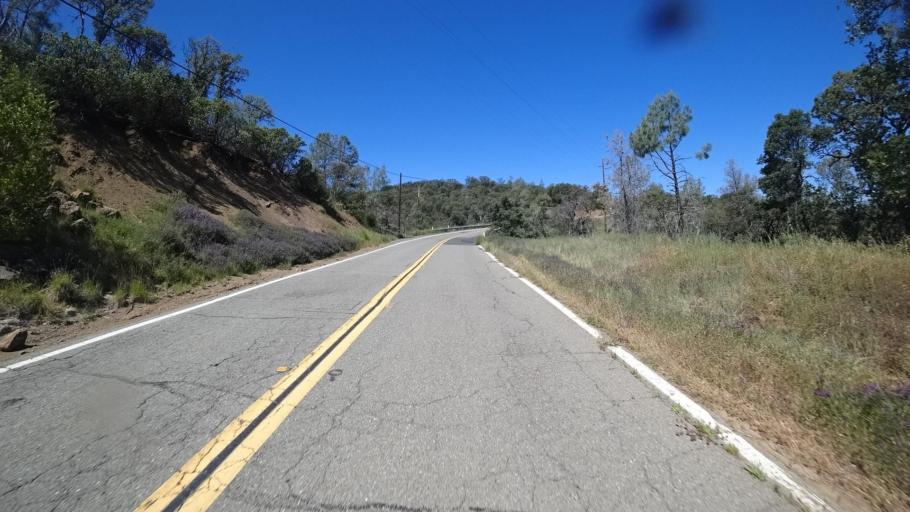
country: US
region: California
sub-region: Lake County
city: Hidden Valley Lake
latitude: 38.8843
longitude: -122.4565
